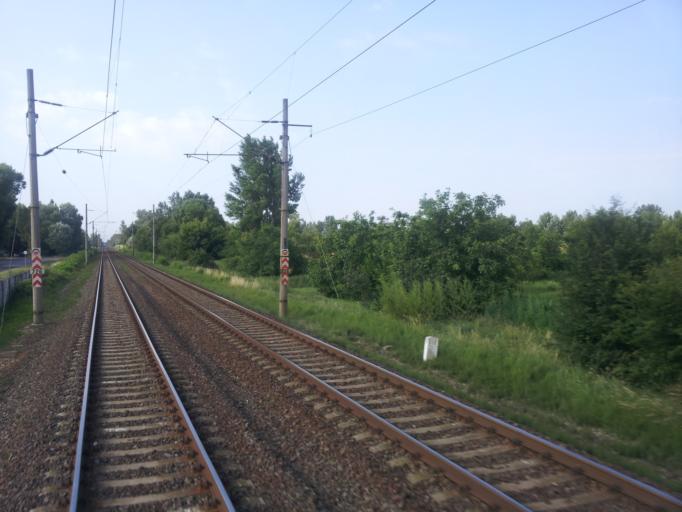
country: HU
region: Fejer
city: Szekesfehervar
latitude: 47.1452
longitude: 18.4077
